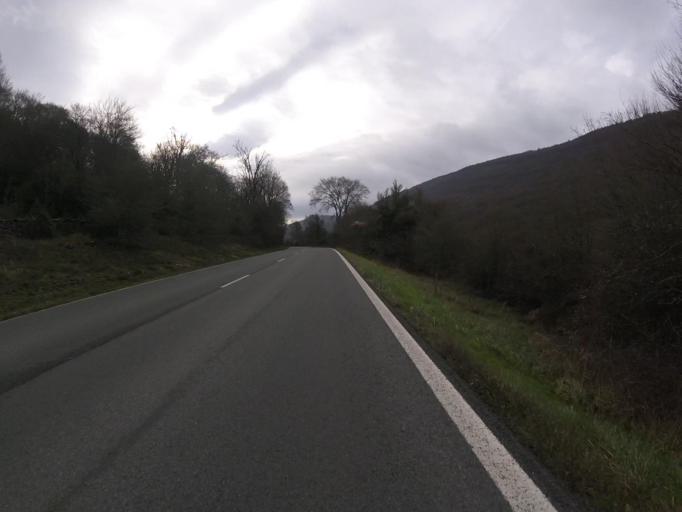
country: ES
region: Navarre
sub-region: Provincia de Navarra
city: Lezaun
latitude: 42.8293
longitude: -2.0280
